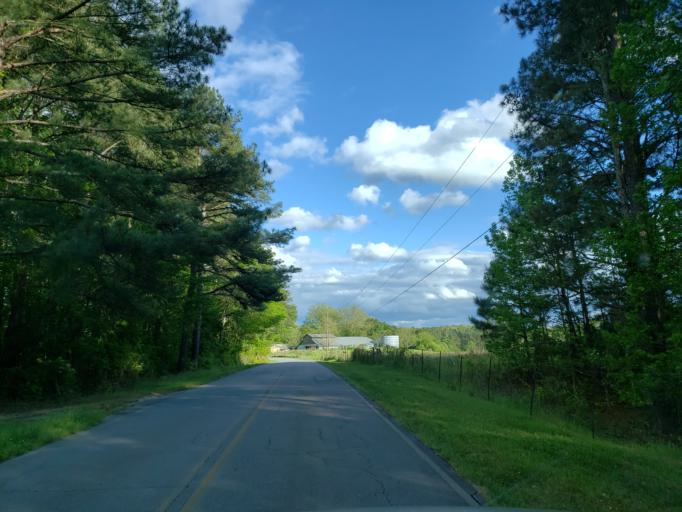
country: US
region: Georgia
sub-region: Haralson County
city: Tallapoosa
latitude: 33.7740
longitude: -85.3055
